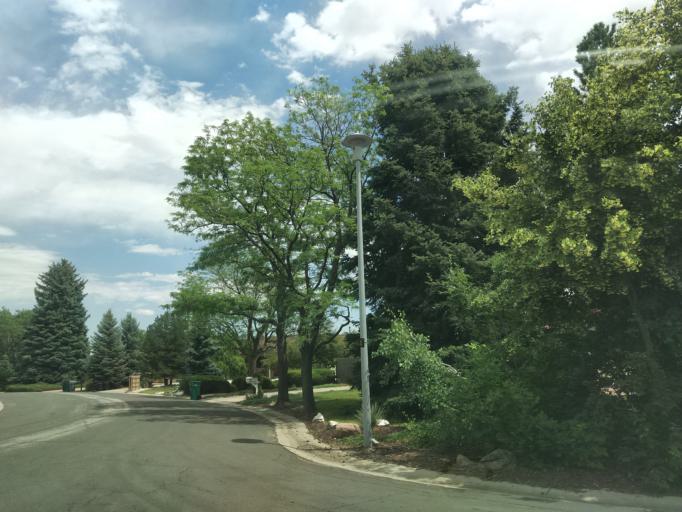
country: US
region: Colorado
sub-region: Jefferson County
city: Lakewood
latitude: 39.6828
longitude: -105.1274
